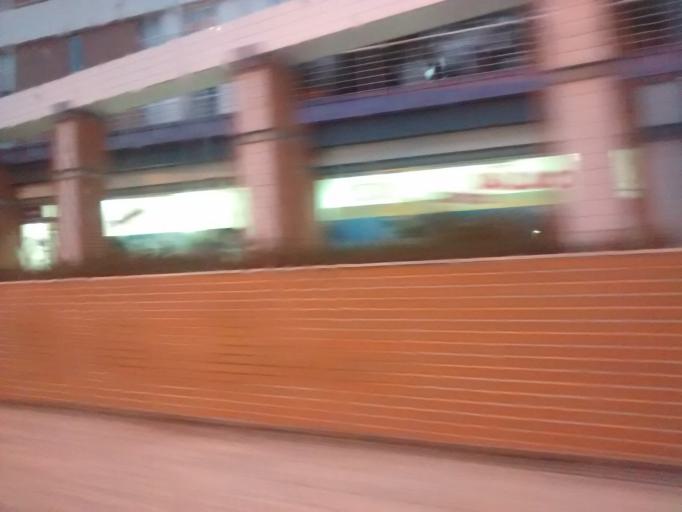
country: PT
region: Aveiro
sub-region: Aveiro
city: Aveiro
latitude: 40.6403
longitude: -8.6486
